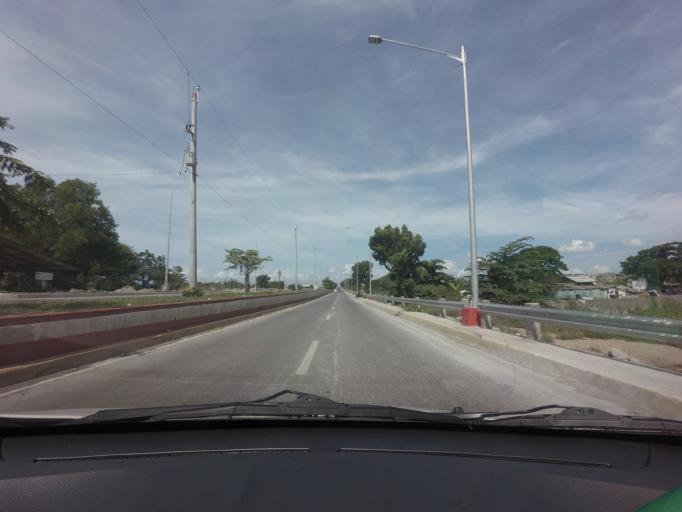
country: PH
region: Calabarzon
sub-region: Province of Rizal
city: Taguig
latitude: 14.5279
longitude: 121.0913
